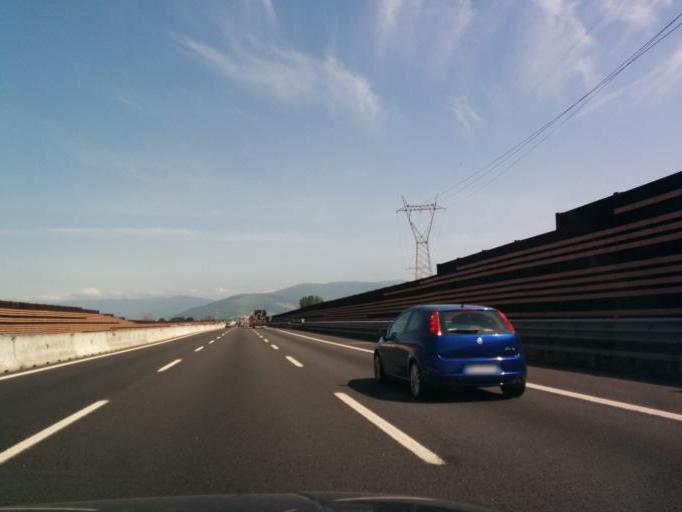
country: IT
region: Tuscany
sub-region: Province of Florence
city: San Donnino
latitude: 43.7951
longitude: 11.1566
